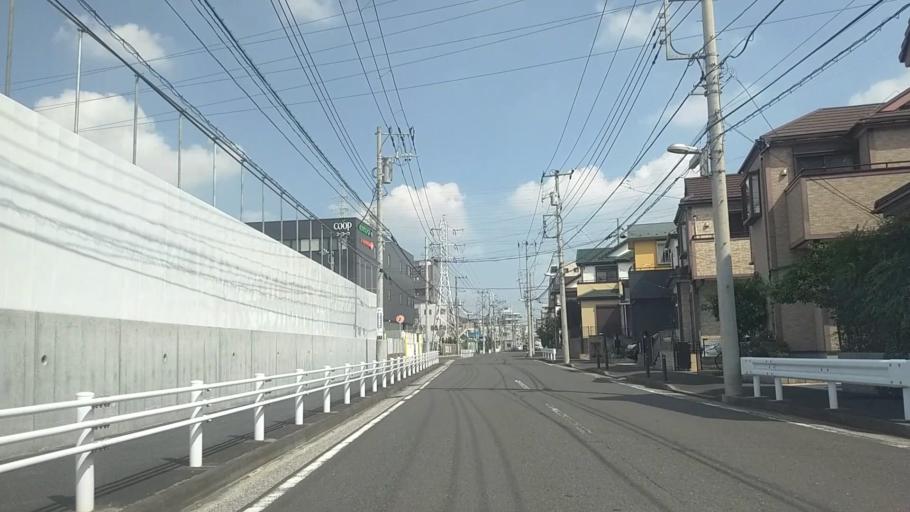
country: JP
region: Kanagawa
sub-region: Kawasaki-shi
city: Kawasaki
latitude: 35.5256
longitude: 139.6793
